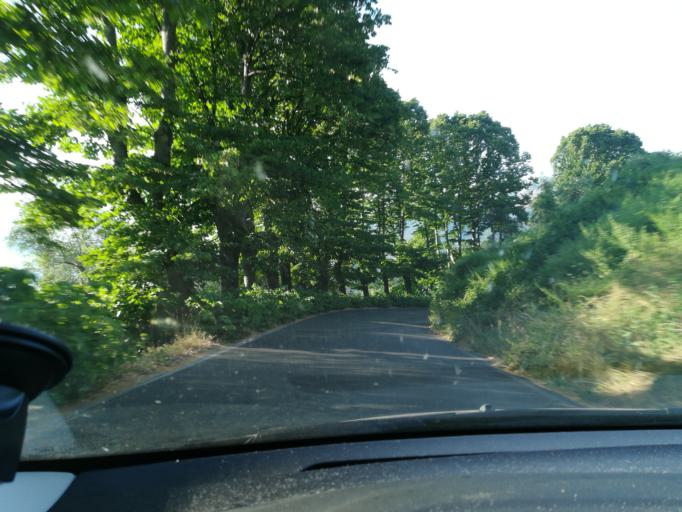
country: IT
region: Tuscany
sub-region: Provincia di Lucca
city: Stiava
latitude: 43.9143
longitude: 10.3381
